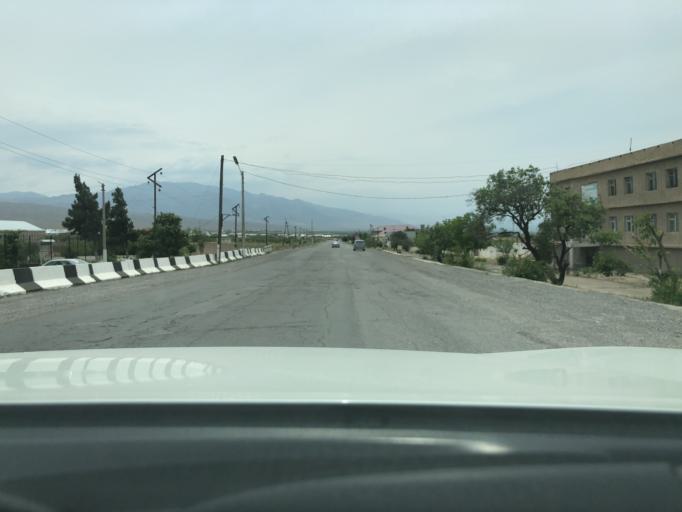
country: TJ
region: Viloyati Sughd
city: Konibodom
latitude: 40.2723
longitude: 70.4368
